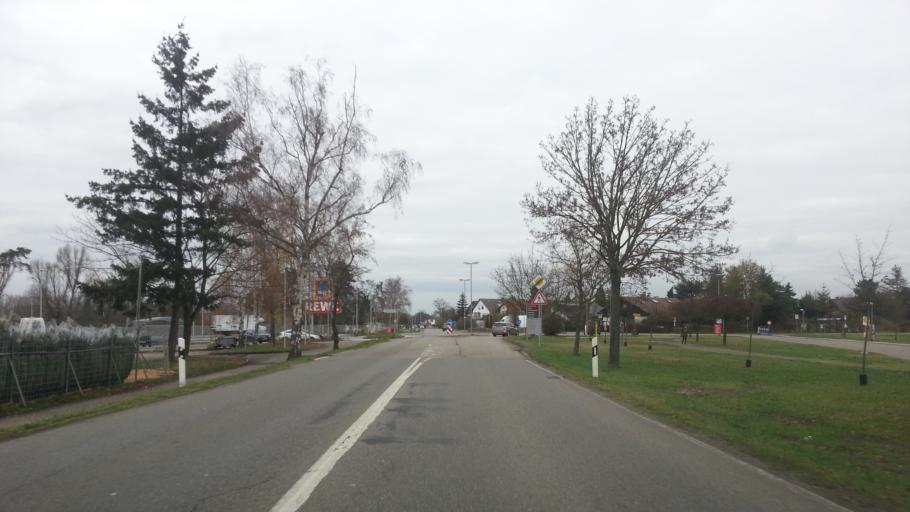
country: DE
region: Baden-Wuerttemberg
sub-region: Karlsruhe Region
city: Ketsch
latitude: 49.3566
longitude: 8.5276
